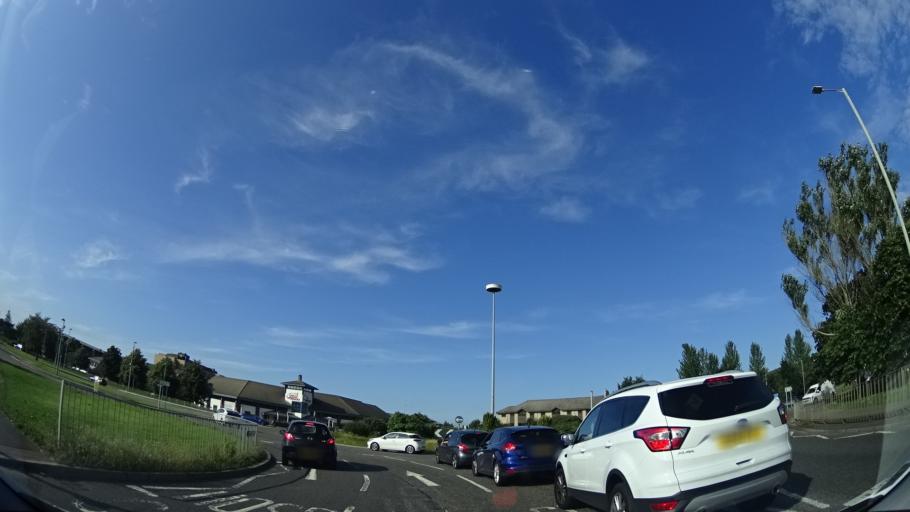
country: GB
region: Scotland
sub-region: Highland
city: Inverness
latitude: 57.4713
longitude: -4.1905
